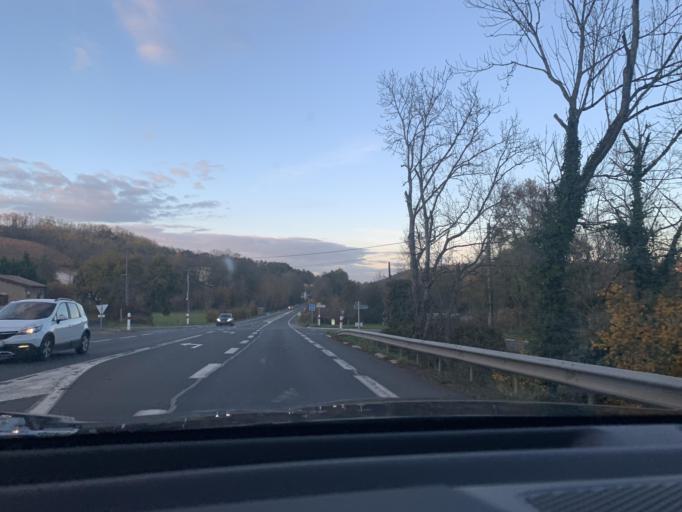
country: FR
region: Rhone-Alpes
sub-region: Departement du Rhone
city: Liergues
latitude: 45.9484
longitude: 4.6619
